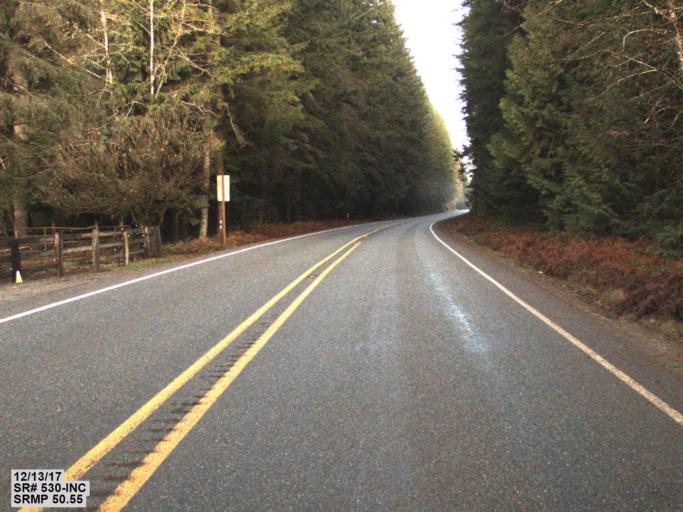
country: US
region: Washington
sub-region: Snohomish County
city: Darrington
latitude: 48.2751
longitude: -121.5938
